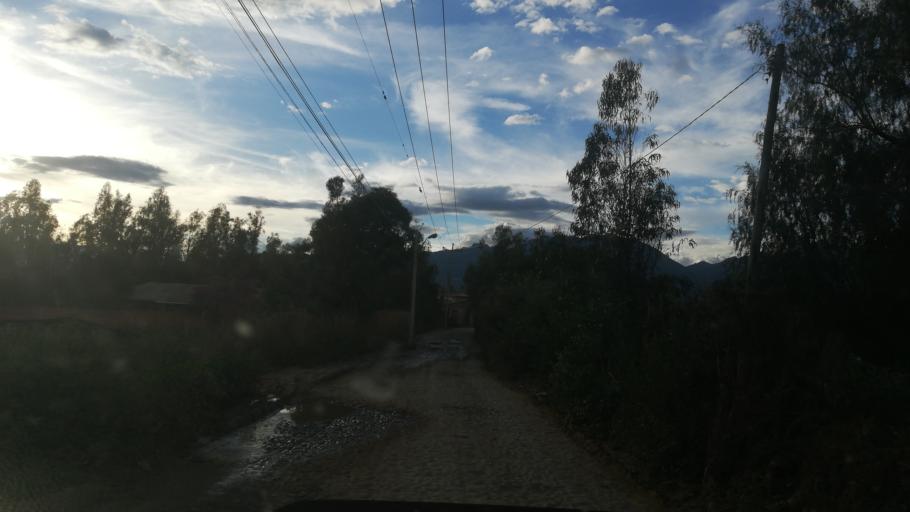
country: BO
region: Cochabamba
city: Cochabamba
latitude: -17.3466
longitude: -66.2241
